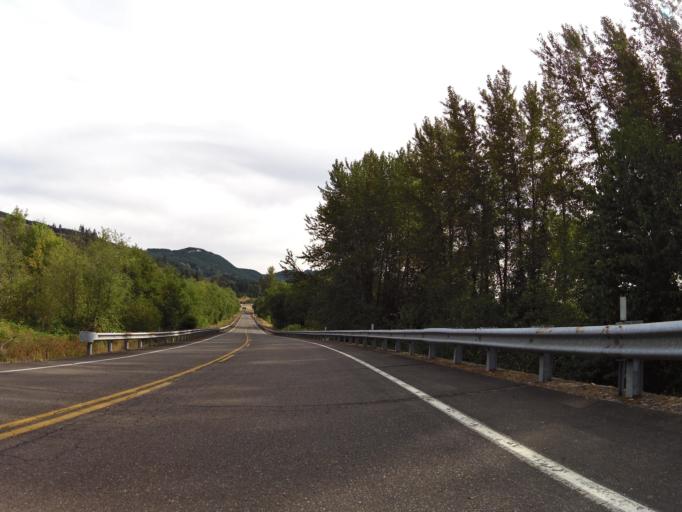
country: US
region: Washington
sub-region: Cowlitz County
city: Castle Rock
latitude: 46.2597
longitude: -122.8889
